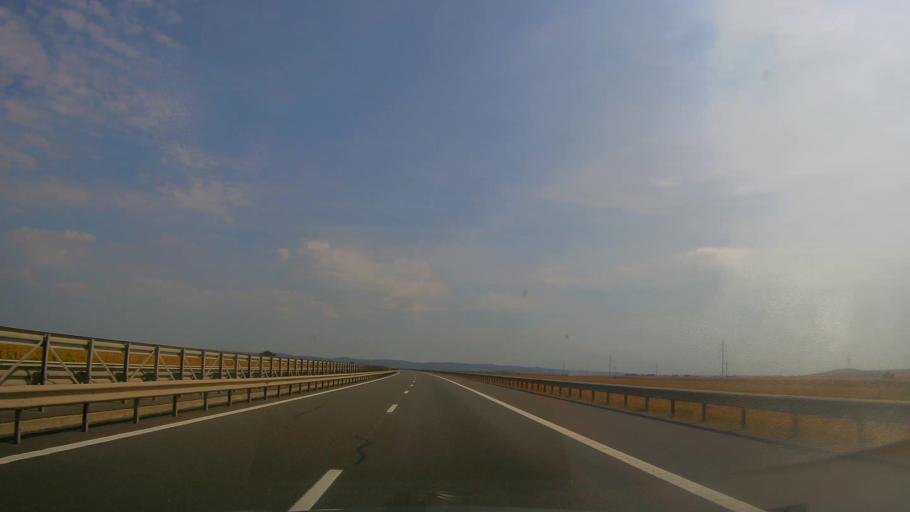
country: RO
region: Cluj
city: Turda
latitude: 46.5234
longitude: 23.8081
